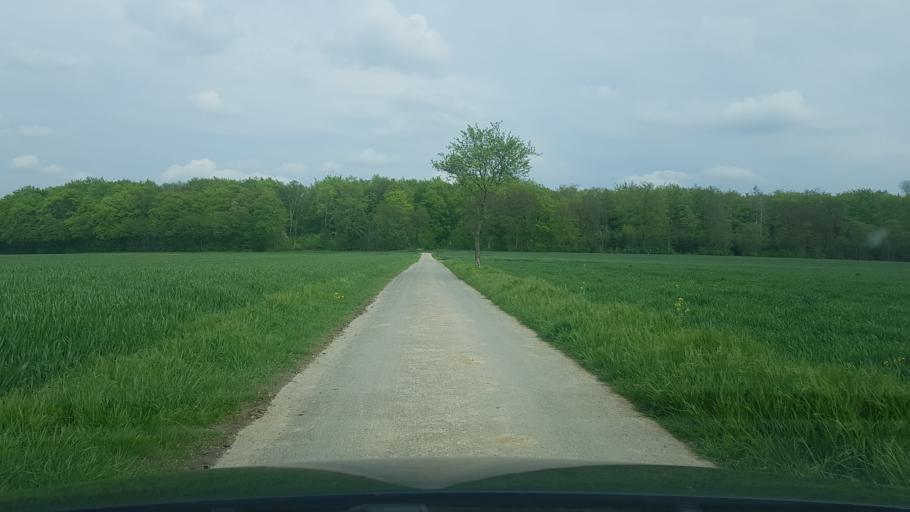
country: DE
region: North Rhine-Westphalia
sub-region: Regierungsbezirk Detmold
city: Paderborn
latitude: 51.6497
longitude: 8.7733
